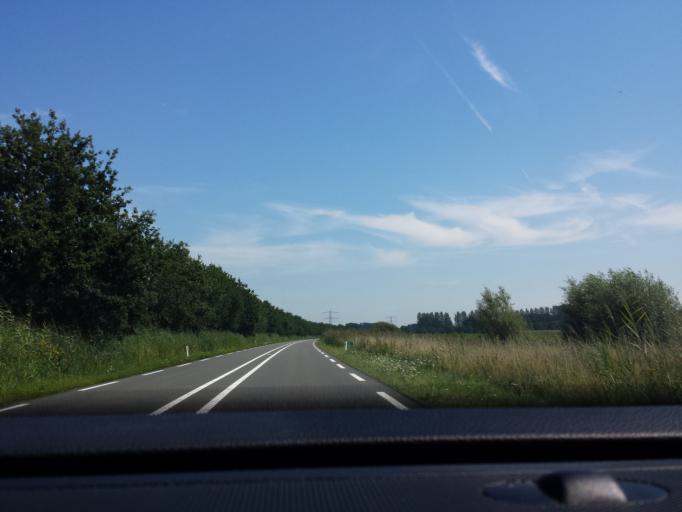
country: NL
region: Overijssel
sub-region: Gemeente Hof van Twente
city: Diepenheim
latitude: 52.2171
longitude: 6.5495
